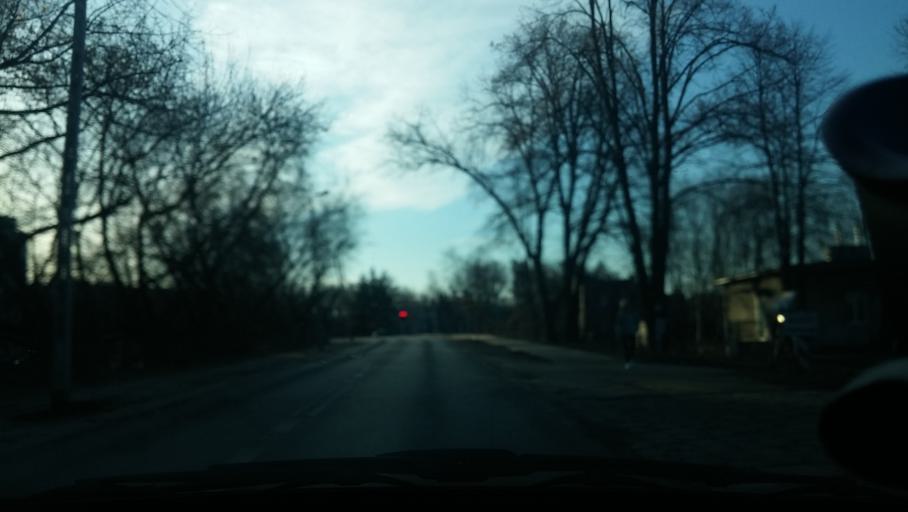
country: PL
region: Masovian Voivodeship
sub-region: Powiat piaseczynski
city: Piaseczno
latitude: 52.0665
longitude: 21.0185
